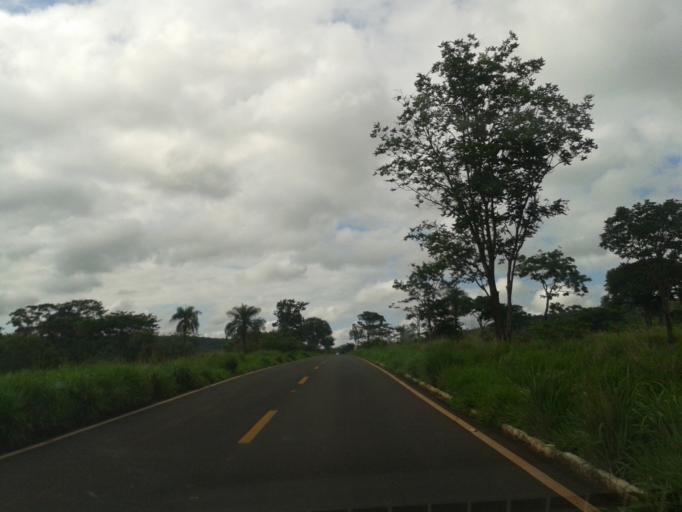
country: BR
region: Minas Gerais
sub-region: Ituiutaba
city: Ituiutaba
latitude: -19.1677
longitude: -49.7800
